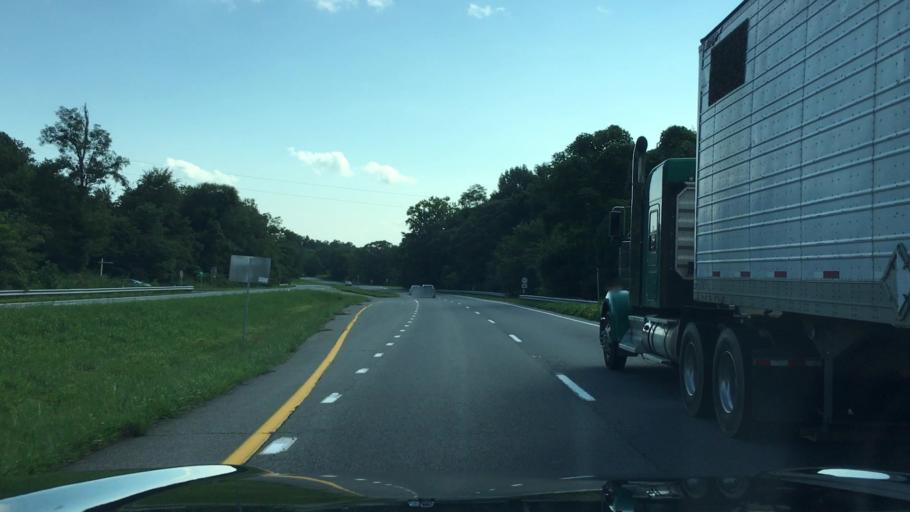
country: US
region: Virginia
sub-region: Nelson County
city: Nellysford
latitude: 37.8850
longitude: -78.7112
